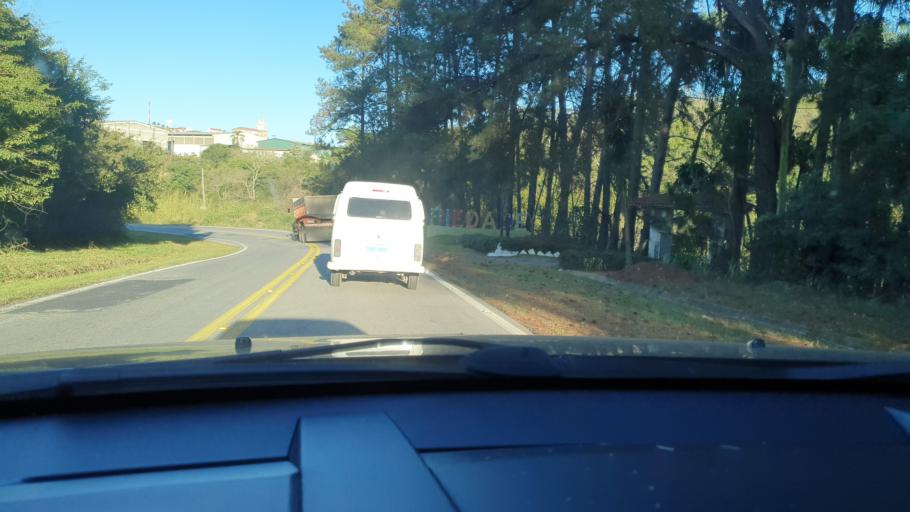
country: BR
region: Sao Paulo
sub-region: Piedade
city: Piedade
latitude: -23.7119
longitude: -47.3986
